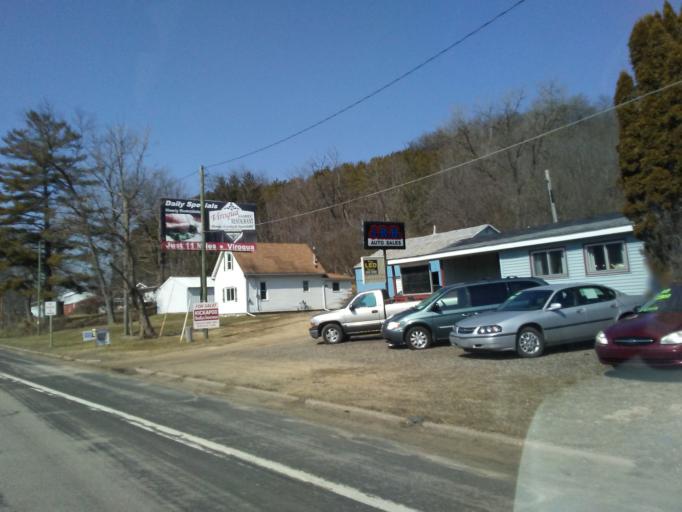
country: US
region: Wisconsin
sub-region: Vernon County
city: Viroqua
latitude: 43.4449
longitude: -90.7684
